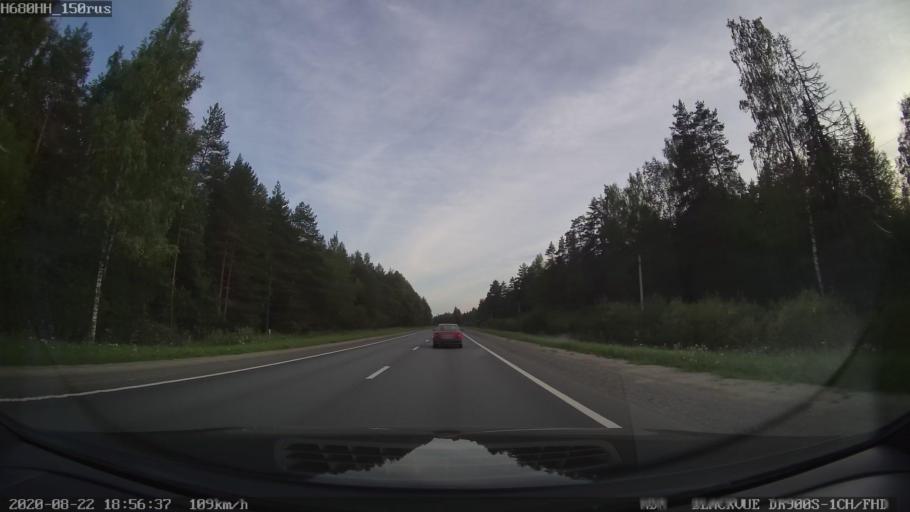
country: RU
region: Tverskaya
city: Rameshki
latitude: 57.1806
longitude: 36.0810
